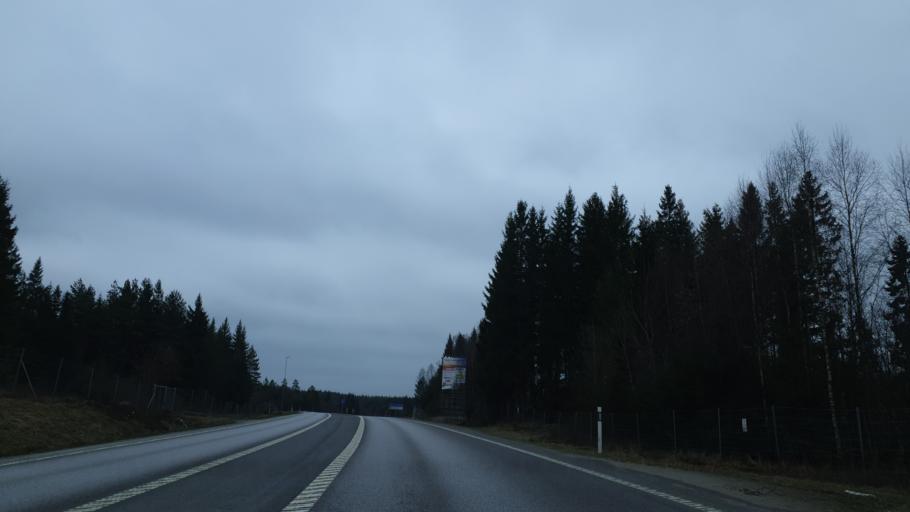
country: SE
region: Vaestra Goetaland
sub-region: Boras Kommun
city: Boras
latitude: 57.6559
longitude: 12.9178
